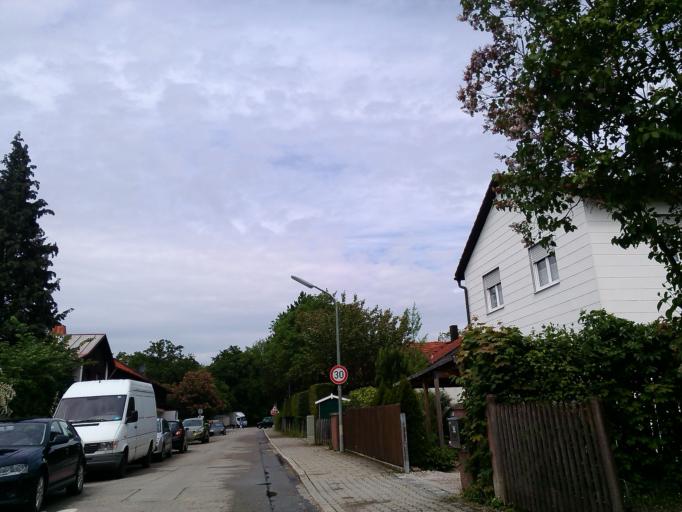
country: DE
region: Bavaria
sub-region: Upper Bavaria
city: Gauting
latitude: 48.0702
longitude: 11.3934
